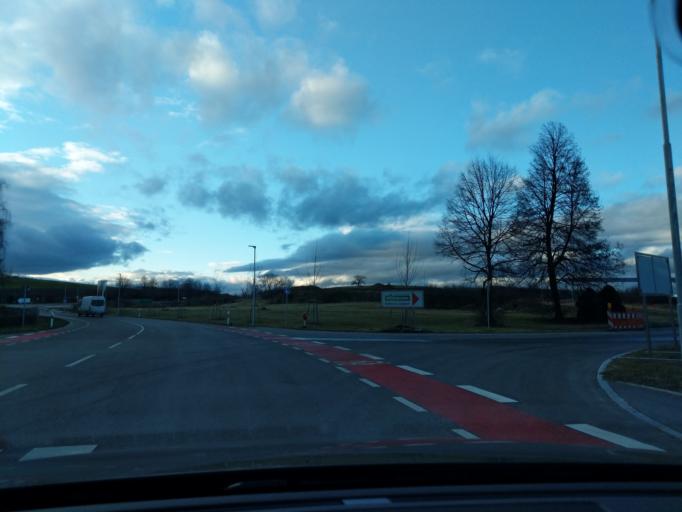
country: DE
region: Baden-Wuerttemberg
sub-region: Tuebingen Region
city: Bermatingen
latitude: 47.7278
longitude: 9.3197
